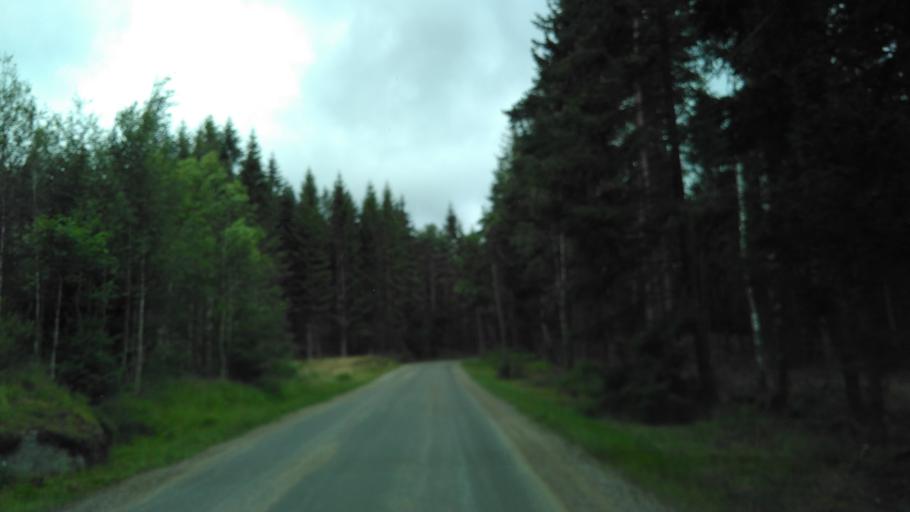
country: SE
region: Vaestra Goetaland
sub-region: Marks Kommun
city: Fritsla
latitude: 57.5728
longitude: 12.7727
